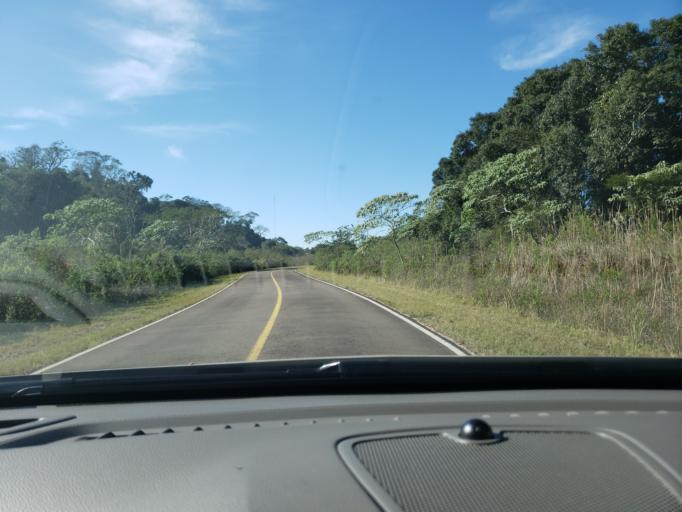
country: BR
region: Rio Grande do Sul
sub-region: Tres Passos
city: Tres Passos
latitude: -27.1527
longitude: -53.9062
